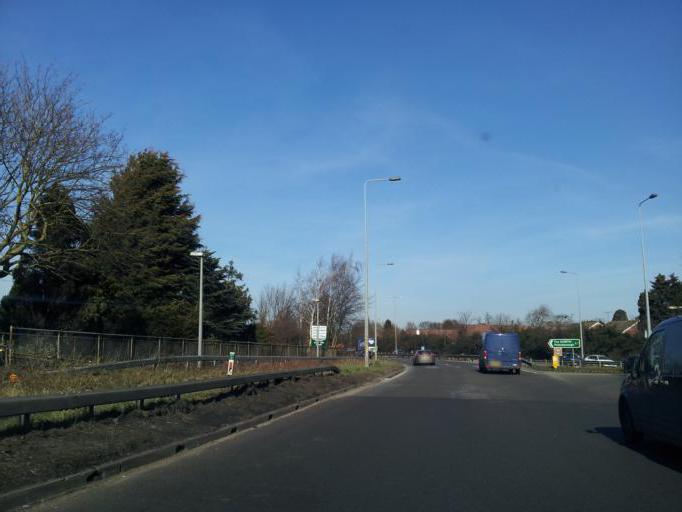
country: GB
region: England
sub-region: Cambridgeshire
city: Buckden
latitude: 52.2917
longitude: -0.2566
